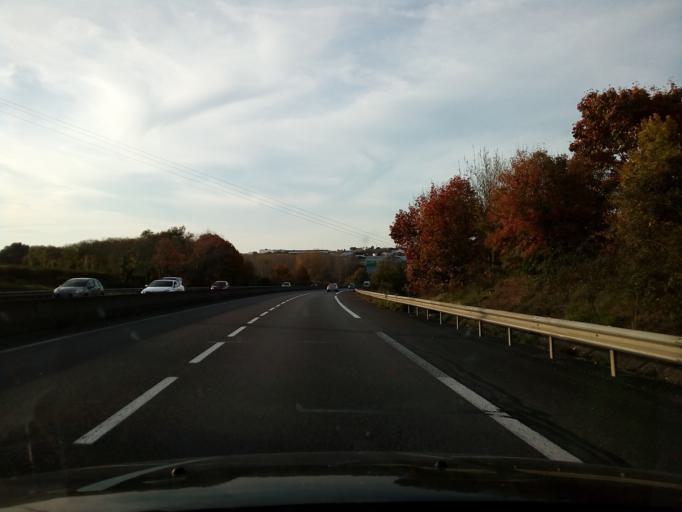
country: FR
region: Poitou-Charentes
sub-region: Departement de la Charente
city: Champniers
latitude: 45.6871
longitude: 0.1979
